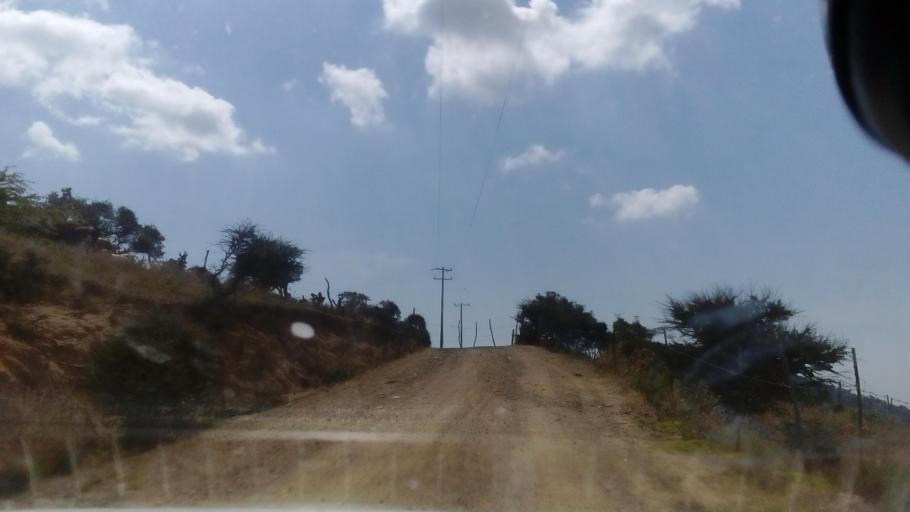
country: MX
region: Guanajuato
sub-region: Silao de la Victoria
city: San Francisco (Banos de Agua Caliente)
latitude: 21.1602
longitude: -101.4604
